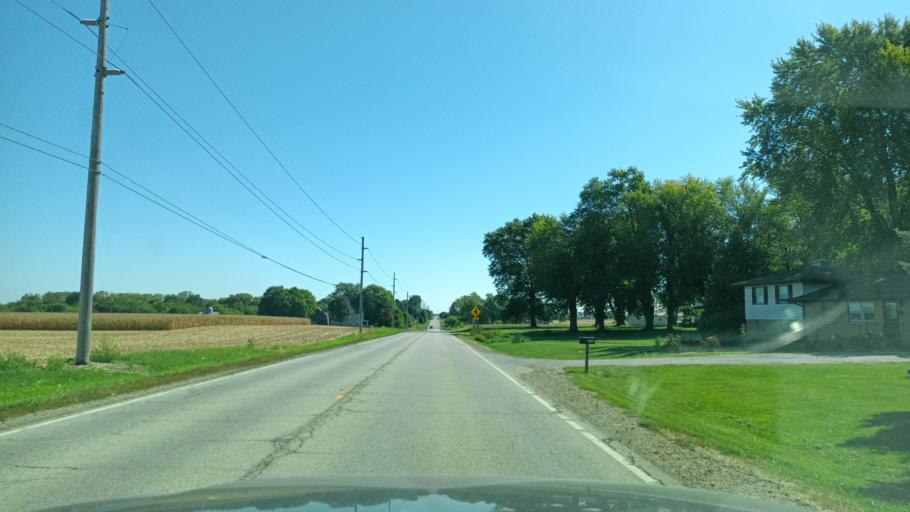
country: US
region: Illinois
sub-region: Peoria County
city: Dunlap
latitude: 40.7851
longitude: -89.7227
